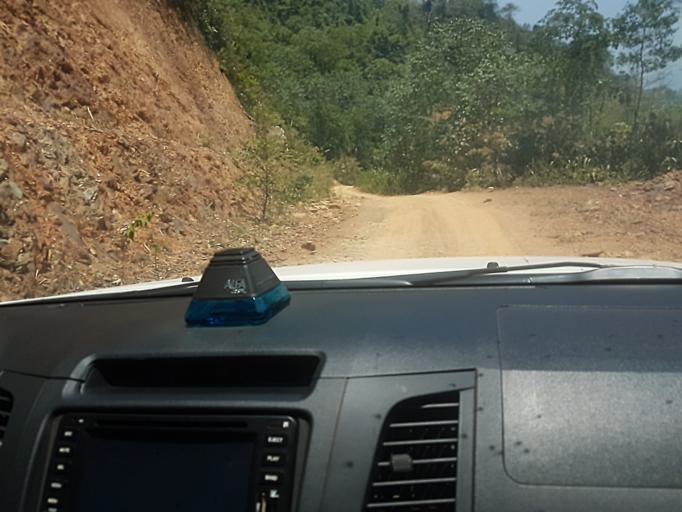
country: VN
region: Nghe An
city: Con Cuong
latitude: 18.6088
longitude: 104.7355
